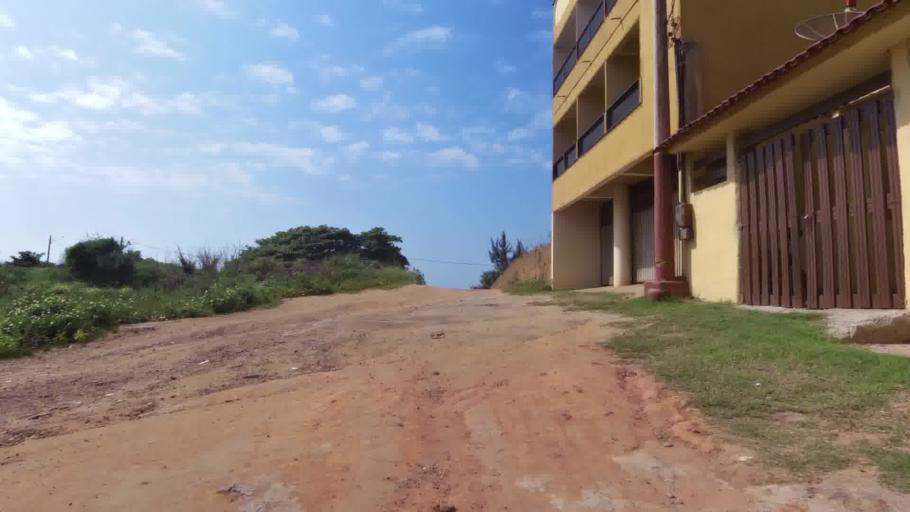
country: BR
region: Espirito Santo
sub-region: Marataizes
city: Marataizes
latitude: -21.0337
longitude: -40.8139
